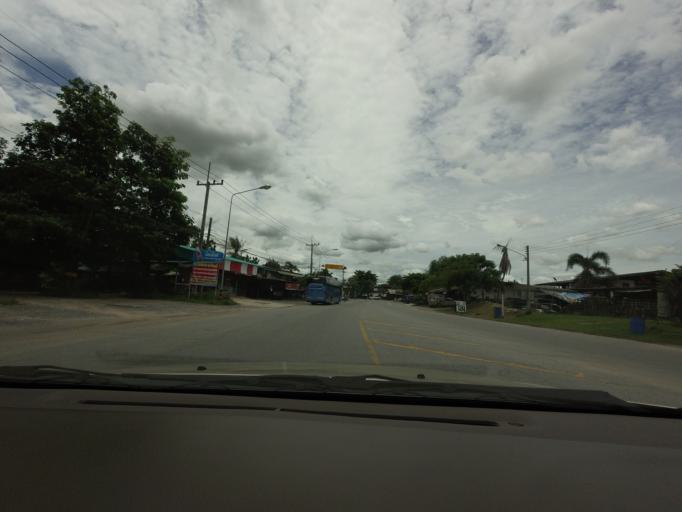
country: TH
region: Chon Buri
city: Si Racha
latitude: 13.2072
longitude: 101.0075
